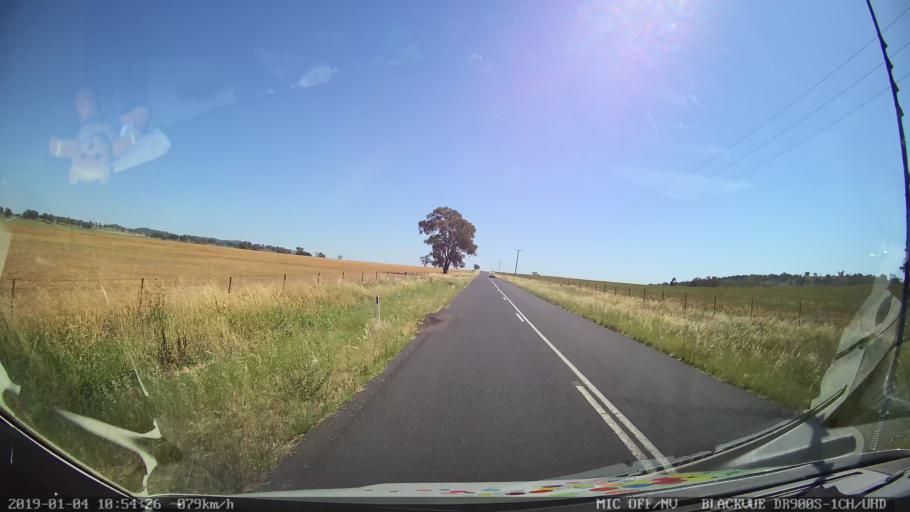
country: AU
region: New South Wales
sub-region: Cabonne
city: Molong
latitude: -33.2053
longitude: 148.6905
